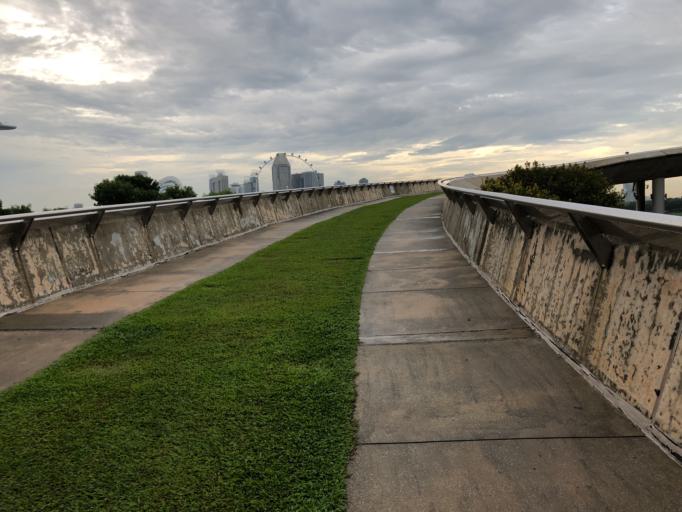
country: SG
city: Singapore
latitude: 1.2805
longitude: 103.8704
